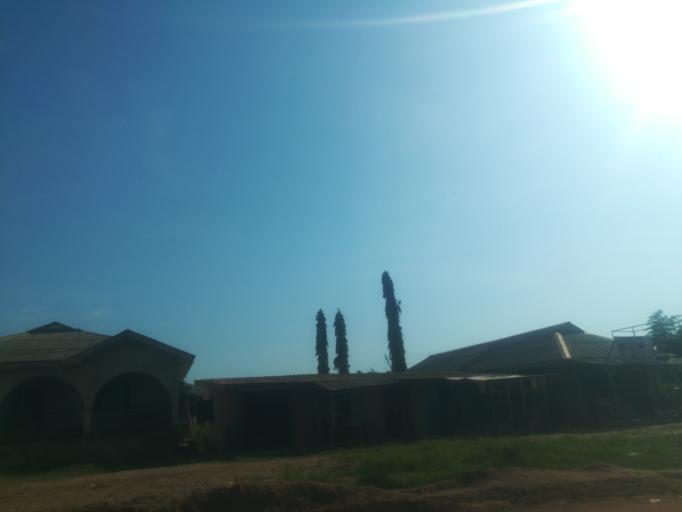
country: NG
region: Ogun
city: Abeokuta
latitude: 7.1406
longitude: 3.2671
